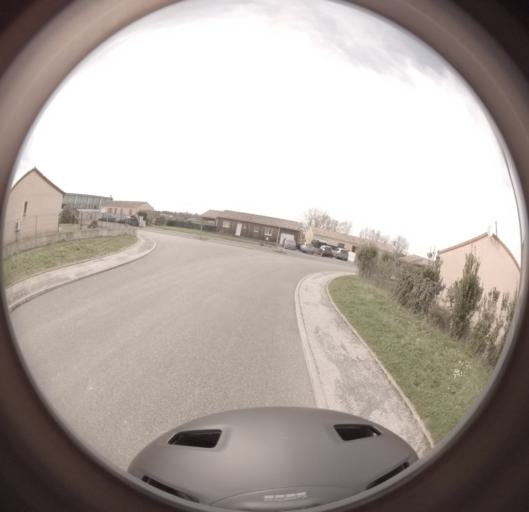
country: FR
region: Midi-Pyrenees
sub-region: Departement du Tarn-et-Garonne
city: Montech
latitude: 43.9600
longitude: 1.2492
